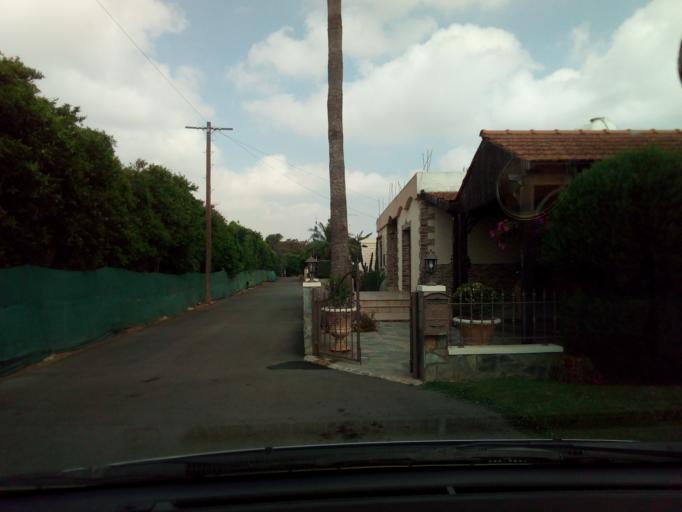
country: CY
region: Ammochostos
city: Avgorou
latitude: 35.0351
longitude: 33.8370
